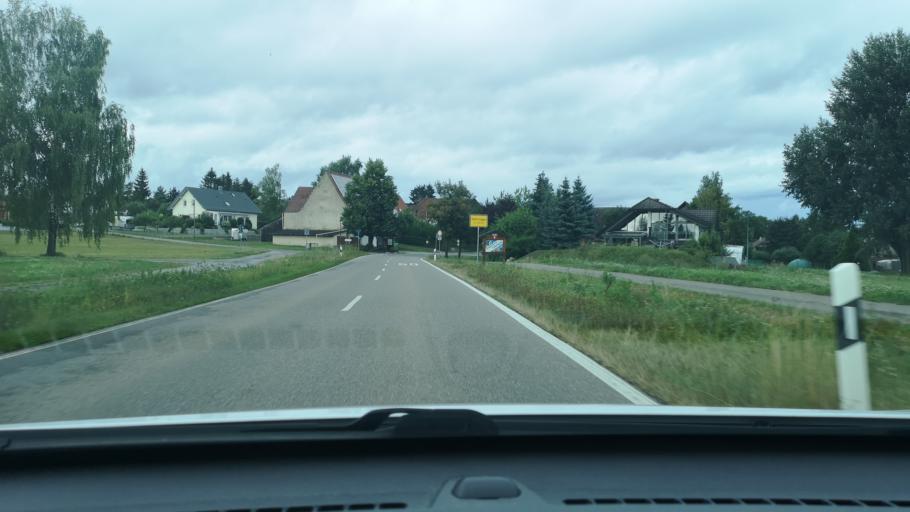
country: DE
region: Baden-Wuerttemberg
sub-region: Freiburg Region
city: Vohringen
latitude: 48.3320
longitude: 8.6563
